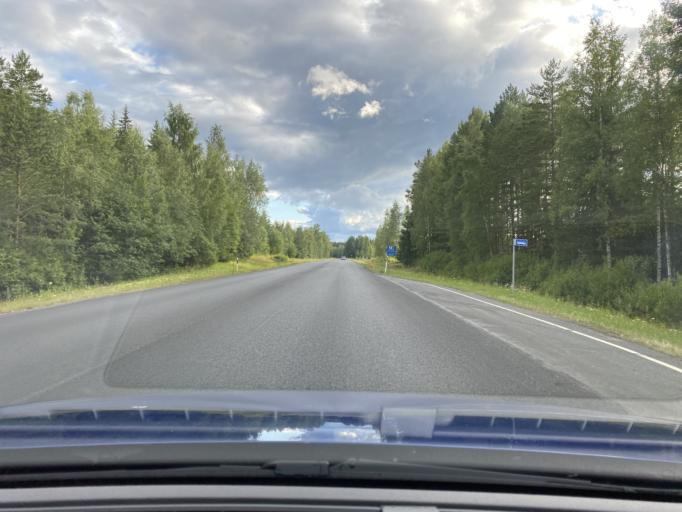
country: FI
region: Haeme
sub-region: Haemeenlinna
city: Renko
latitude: 60.9288
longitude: 24.3526
